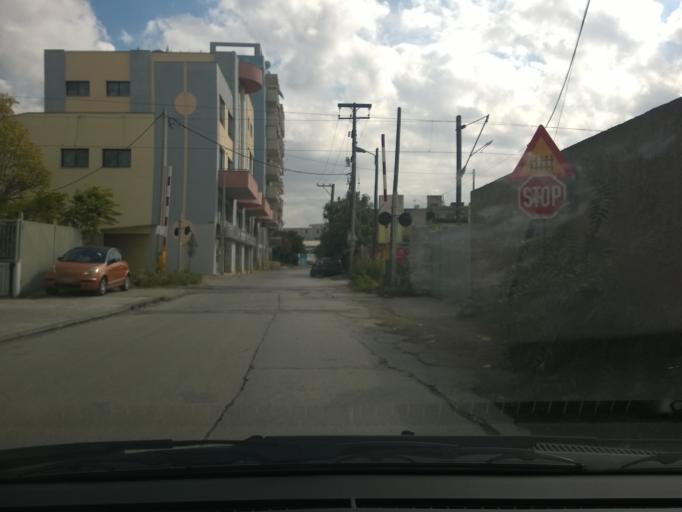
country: GR
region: Central Macedonia
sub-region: Nomos Thessalonikis
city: Menemeni
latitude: 40.6528
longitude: 22.9080
